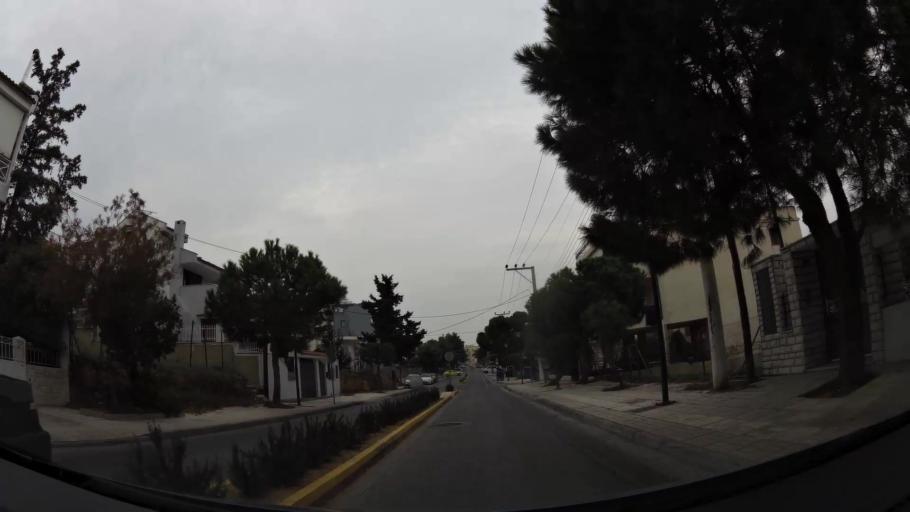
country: GR
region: Attica
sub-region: Nomarchia Athinas
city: Alimos
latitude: 37.9107
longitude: 23.7345
